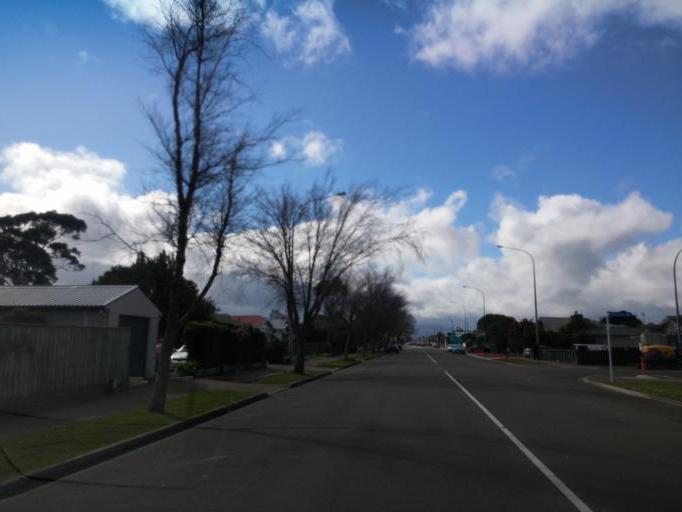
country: NZ
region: Manawatu-Wanganui
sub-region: Palmerston North City
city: Palmerston North
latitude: -40.3642
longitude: 175.6029
